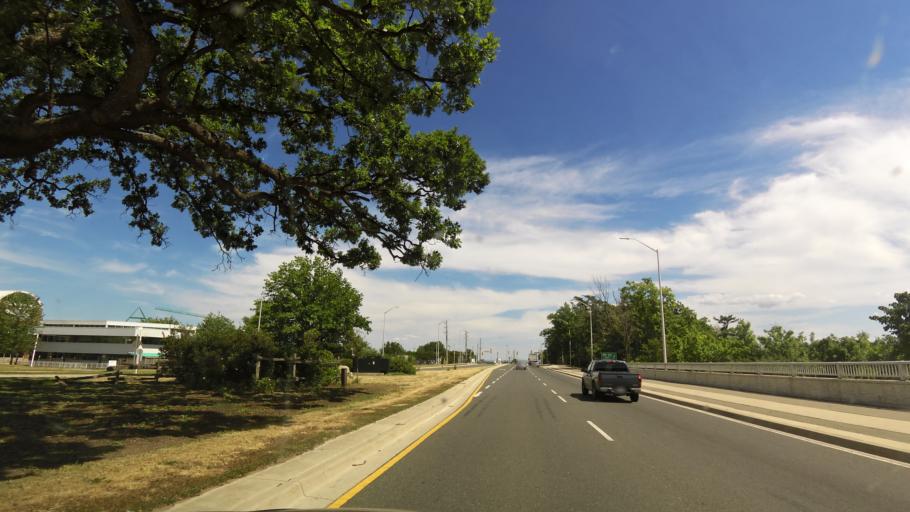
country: CA
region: Ontario
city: Oakville
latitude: 43.4142
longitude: -79.7465
